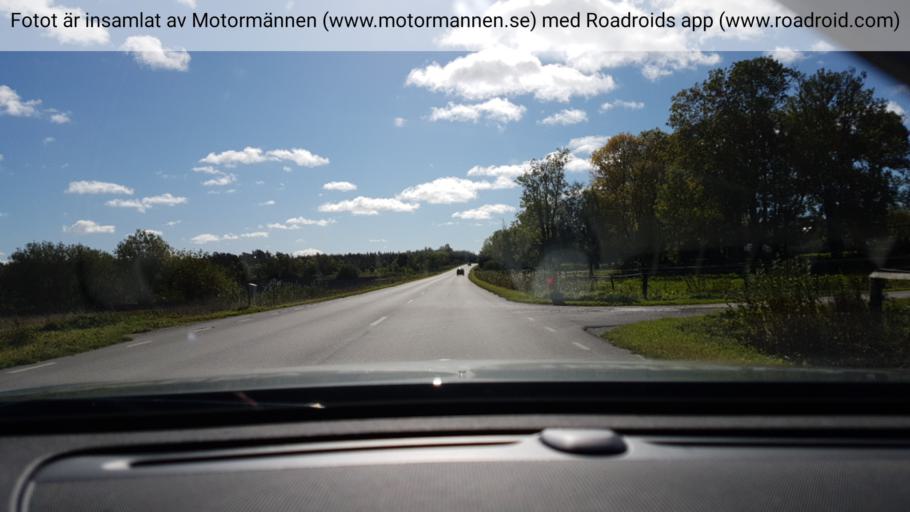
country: SE
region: Gotland
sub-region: Gotland
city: Slite
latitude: 57.7623
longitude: 18.7897
